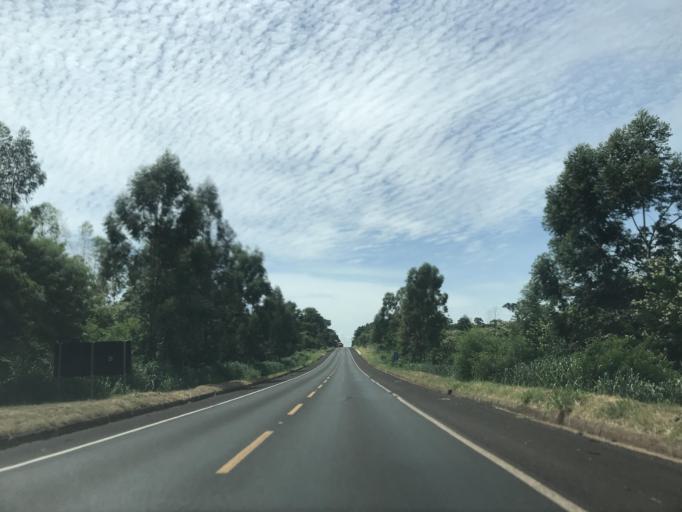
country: BR
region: Parana
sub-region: Paranavai
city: Paranavai
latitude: -23.0178
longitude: -52.5055
